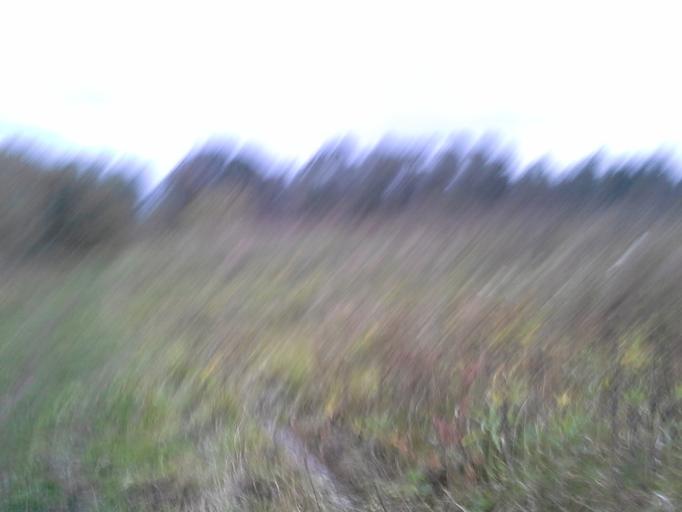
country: RU
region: Moskovskaya
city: Kokoshkino
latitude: 55.6107
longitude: 37.1464
